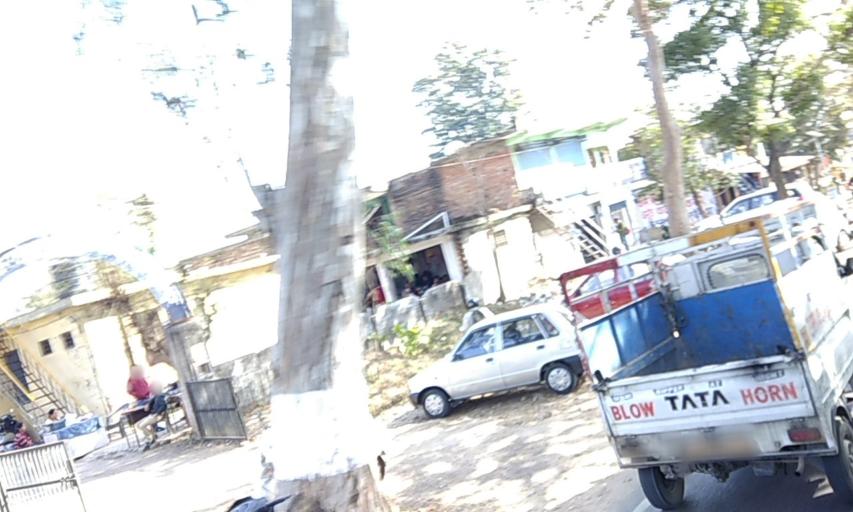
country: IN
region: Himachal Pradesh
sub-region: Kangra
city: Yol
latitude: 32.2172
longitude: 76.1789
